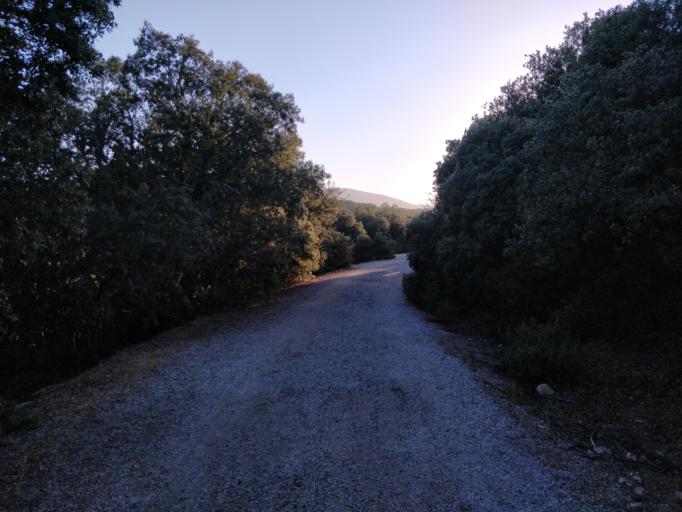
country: ES
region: Madrid
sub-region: Provincia de Madrid
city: Cervera de Buitrago
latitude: 40.9095
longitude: -3.5504
